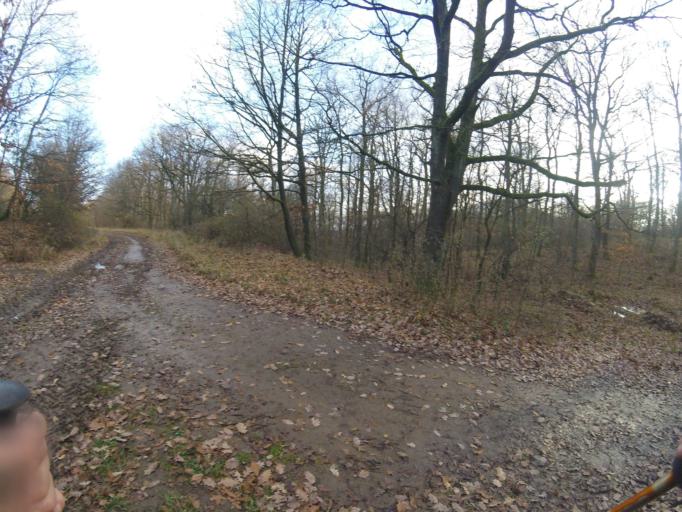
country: HU
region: Pest
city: Szob
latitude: 47.8889
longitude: 18.8887
